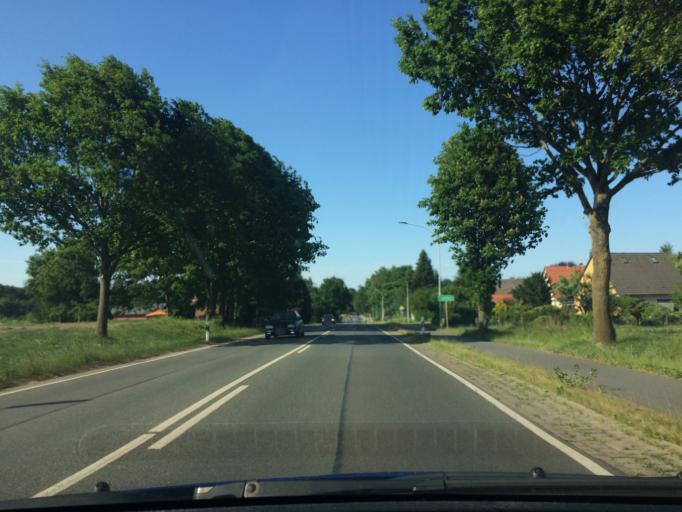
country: DE
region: Lower Saxony
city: Soltau
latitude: 53.0067
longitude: 9.8418
